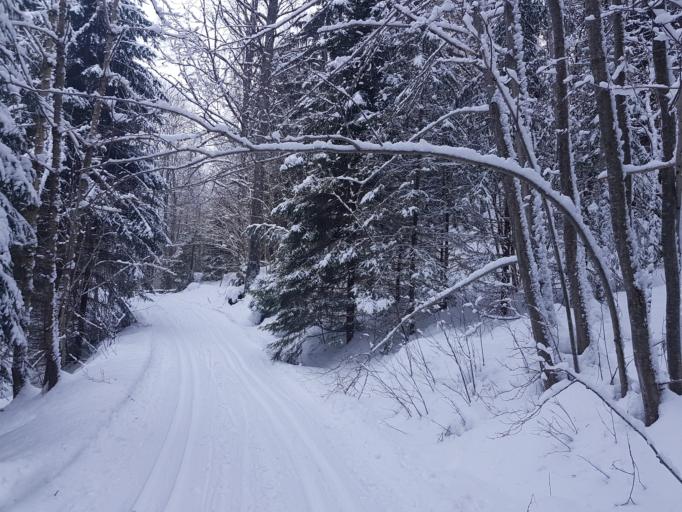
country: NO
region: Akershus
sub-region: Lorenskog
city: Kjenn
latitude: 59.8974
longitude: 10.8749
